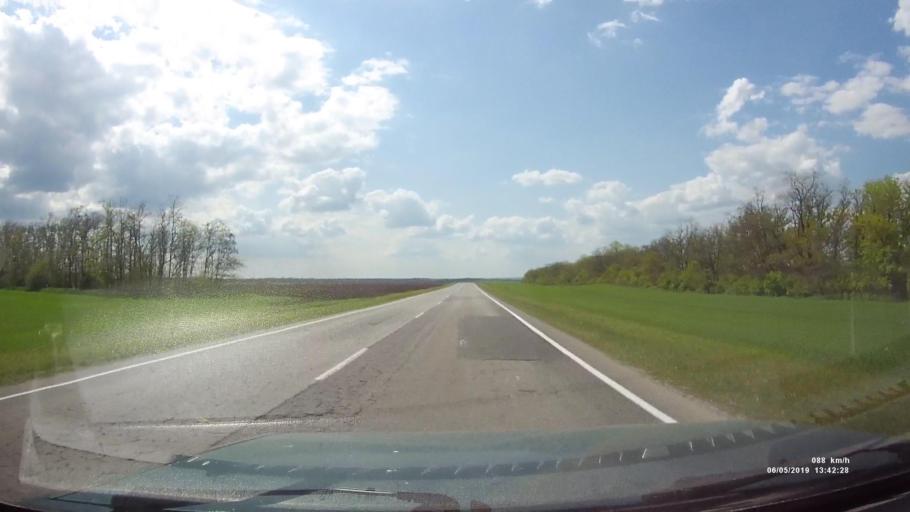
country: RU
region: Rostov
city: Semikarakorsk
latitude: 47.6593
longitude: 40.6565
